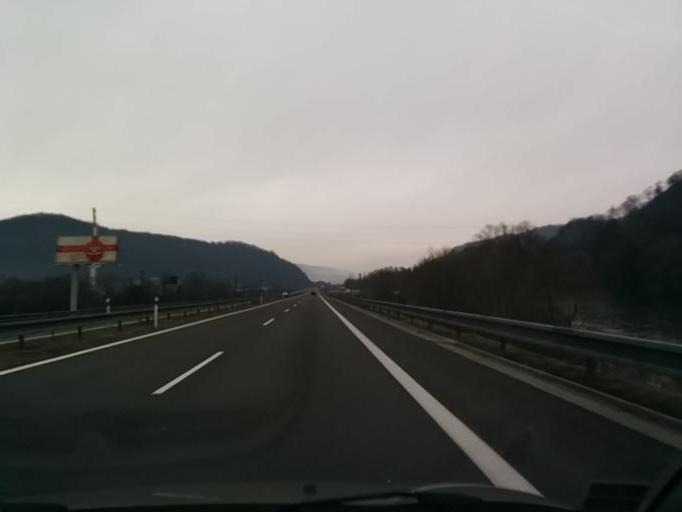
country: SK
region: Banskobystricky
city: Zarnovica
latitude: 48.4841
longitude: 18.7303
